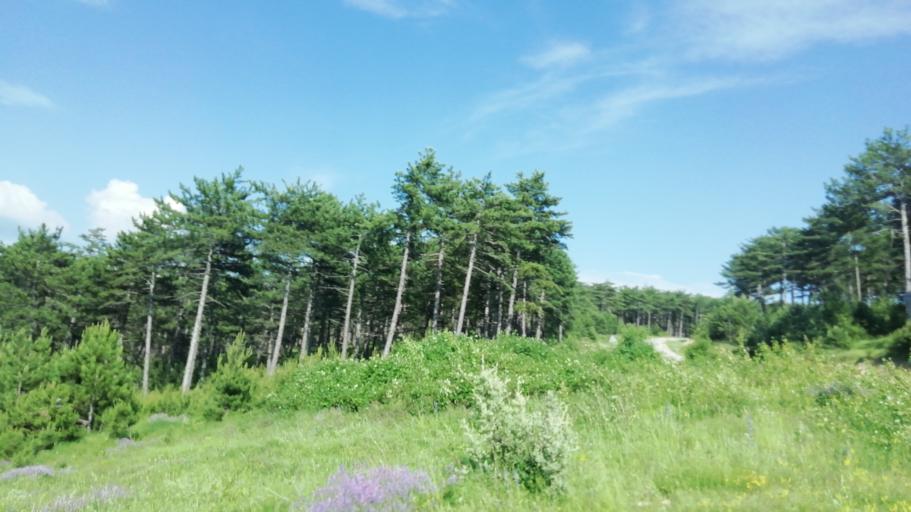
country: TR
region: Karabuk
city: Karabuk
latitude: 41.1165
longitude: 32.6035
